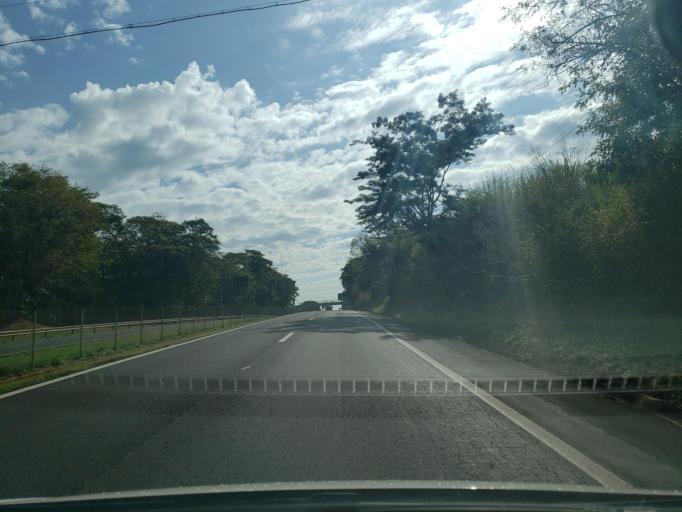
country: BR
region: Sao Paulo
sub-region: Lins
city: Lins
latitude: -21.6876
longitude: -49.7600
